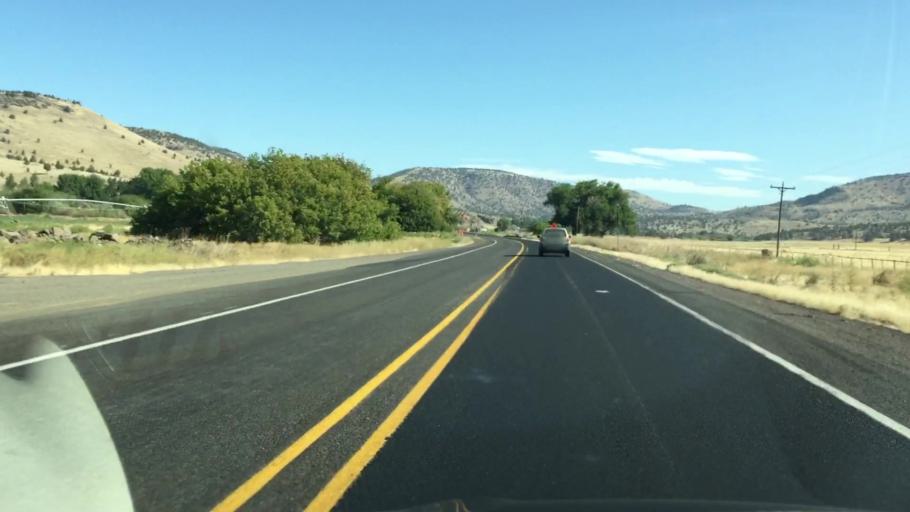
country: US
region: Oregon
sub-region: Jefferson County
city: Madras
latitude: 44.8052
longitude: -120.9375
